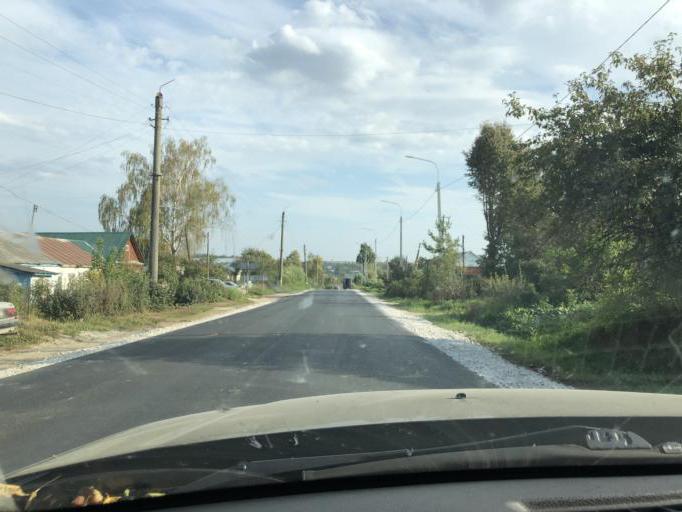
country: RU
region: Tula
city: Leninskiy
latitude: 54.2962
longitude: 37.4602
